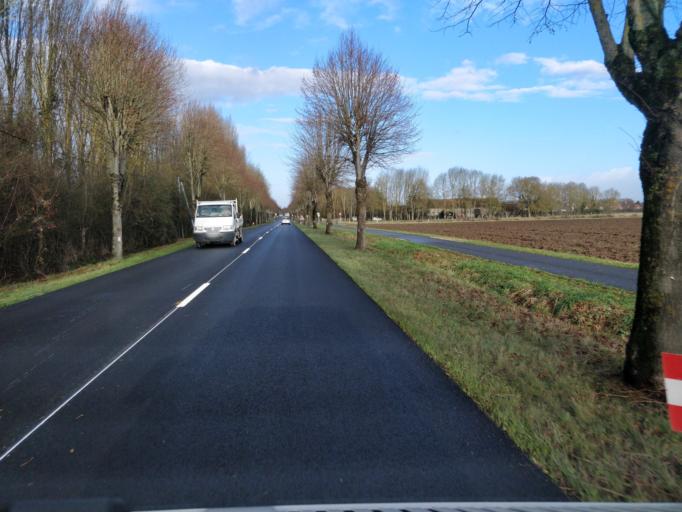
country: FR
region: Centre
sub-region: Departement du Loir-et-Cher
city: Muides-sur-Loire
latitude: 47.6867
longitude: 1.5170
